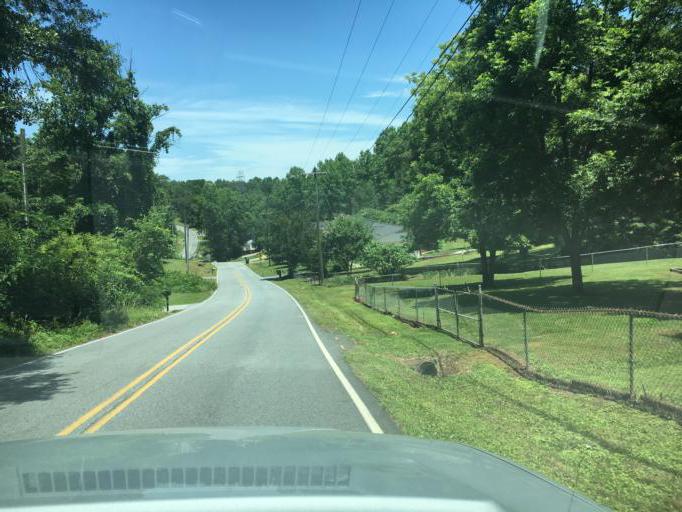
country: US
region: South Carolina
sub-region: Greenville County
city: Greer
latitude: 34.9558
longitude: -82.2243
